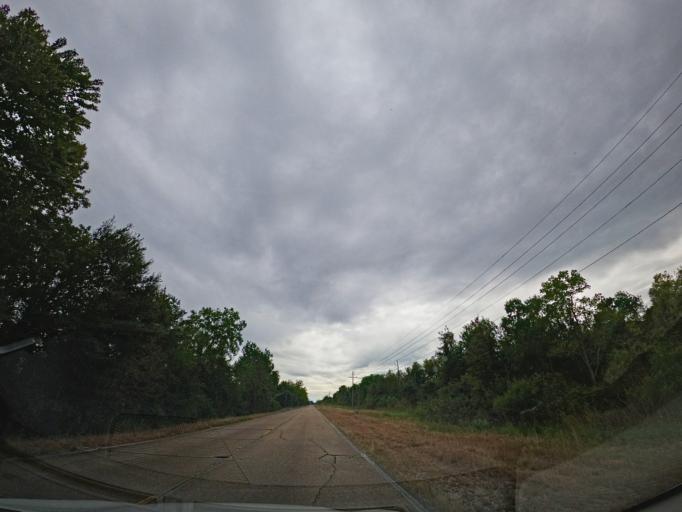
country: US
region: Mississippi
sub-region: Hancock County
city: Pearlington
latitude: 30.2200
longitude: -89.6859
